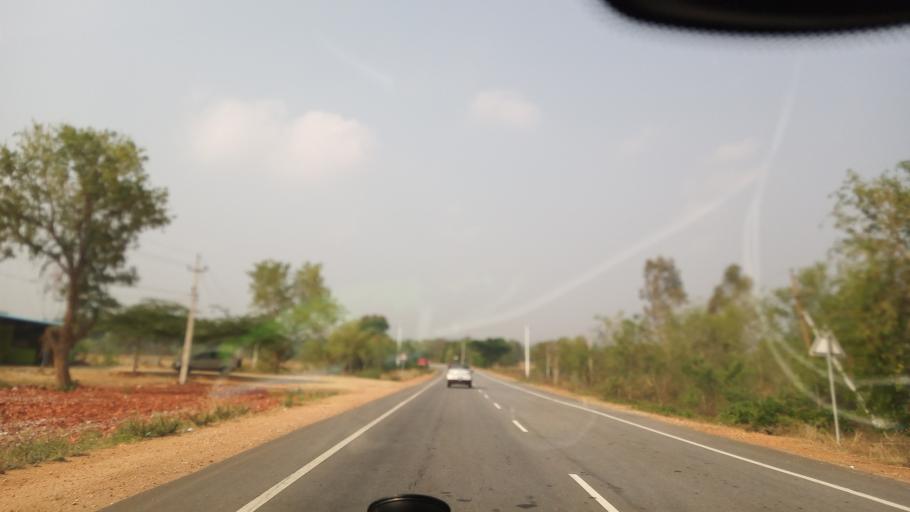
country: IN
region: Karnataka
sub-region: Mandya
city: Nagamangala
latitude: 12.7792
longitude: 76.7431
